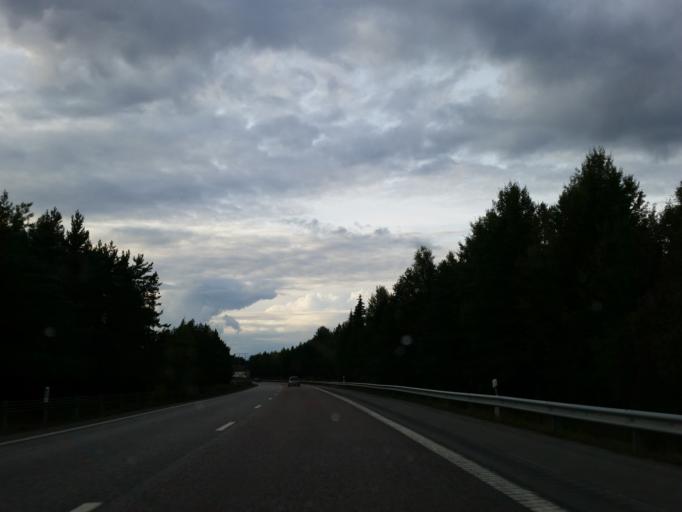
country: SE
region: Uppsala
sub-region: Knivsta Kommun
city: Knivsta
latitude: 59.7558
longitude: 17.8062
